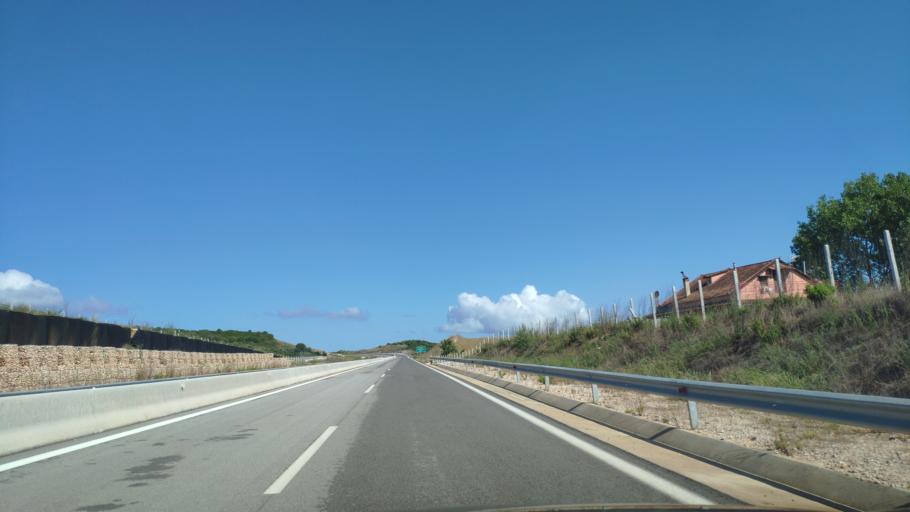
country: GR
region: West Greece
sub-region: Nomos Aitolias kai Akarnanias
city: Vonitsa
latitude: 38.9112
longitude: 20.8308
